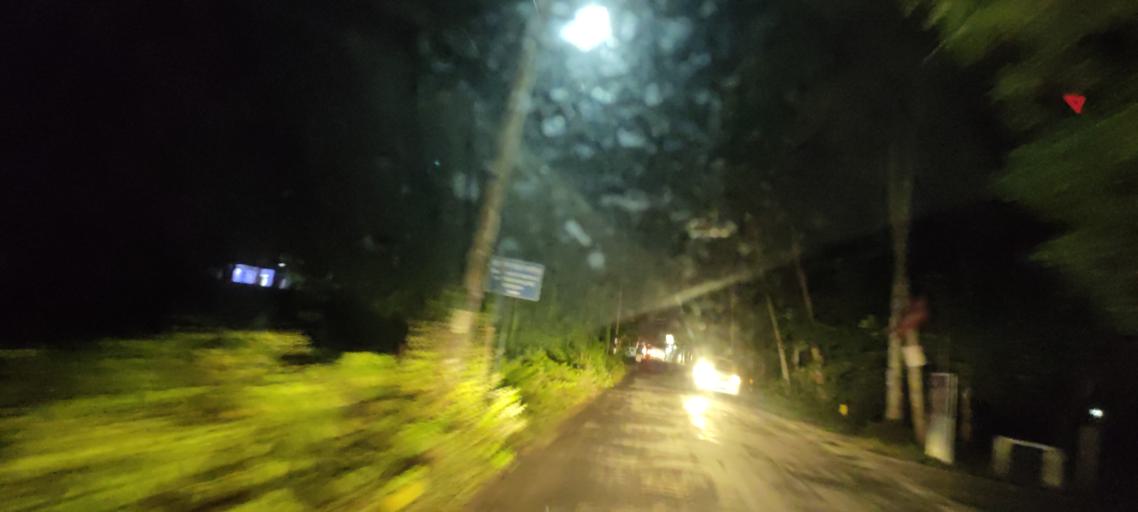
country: IN
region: Kerala
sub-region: Alappuzha
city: Vayalar
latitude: 9.7233
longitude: 76.3228
